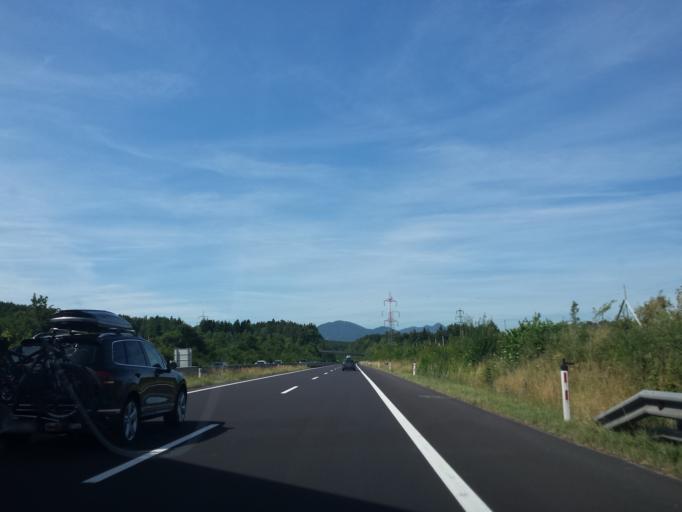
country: AT
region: Lower Austria
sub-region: Politischer Bezirk Neunkirchen
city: Wimpassing im Schwarzatale
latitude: 47.6858
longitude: 16.0413
